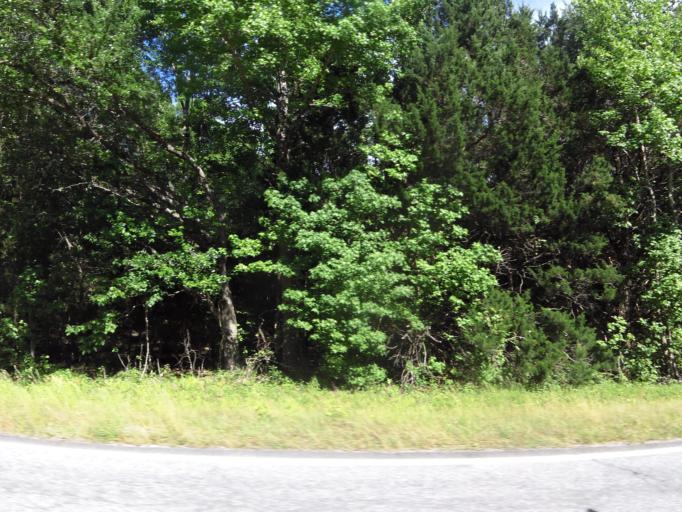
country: US
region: South Carolina
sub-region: Bamberg County
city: Denmark
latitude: 33.1751
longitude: -81.1869
